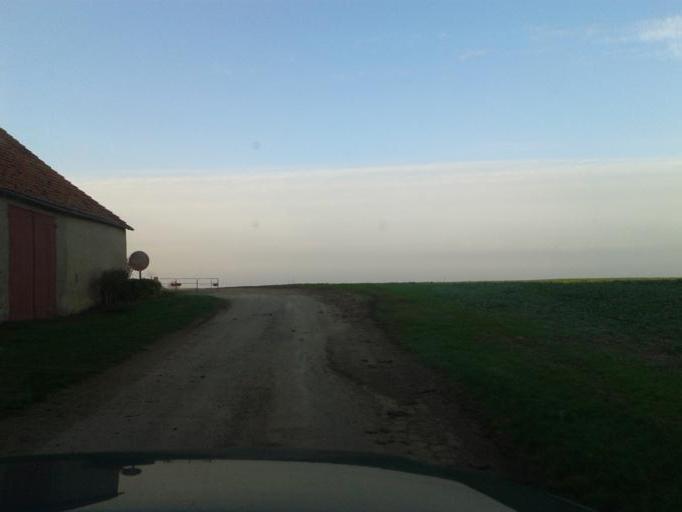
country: FR
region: Centre
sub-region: Departement du Loiret
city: Tavers
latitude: 47.7686
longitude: 1.5815
